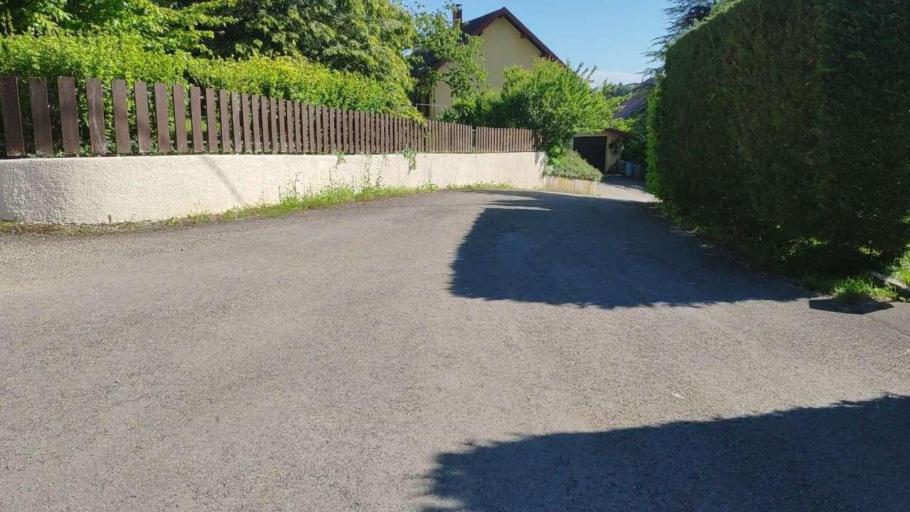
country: FR
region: Franche-Comte
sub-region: Departement du Jura
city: Perrigny
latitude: 46.7230
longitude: 5.5787
